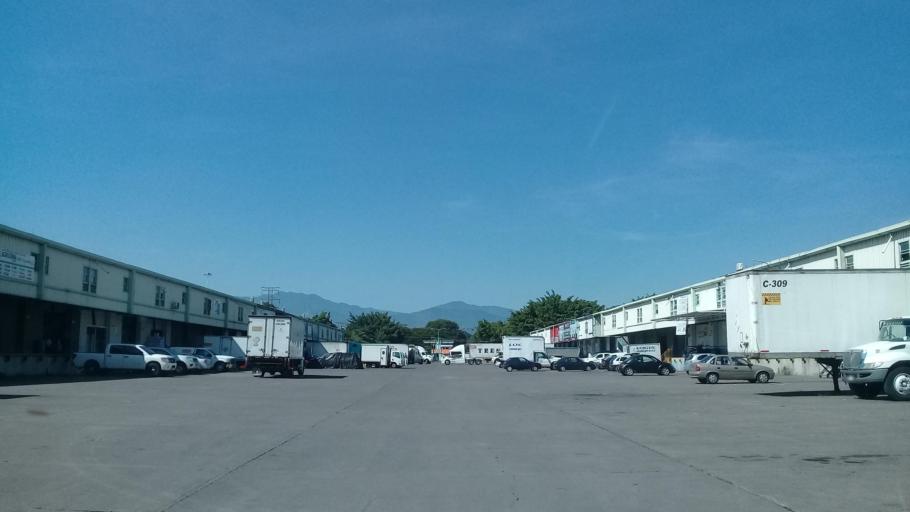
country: MX
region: Veracruz
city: Amatlan de los Reyes
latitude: 18.8575
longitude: -96.9100
